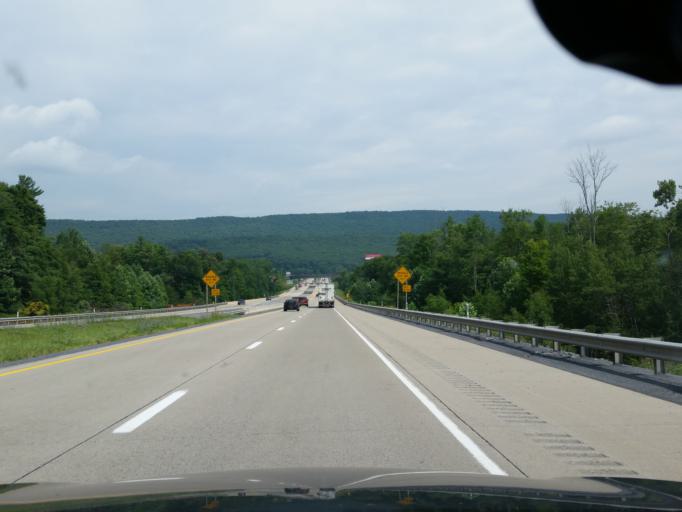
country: US
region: Pennsylvania
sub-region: Mifflin County
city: Milroy
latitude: 40.7159
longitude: -77.6005
